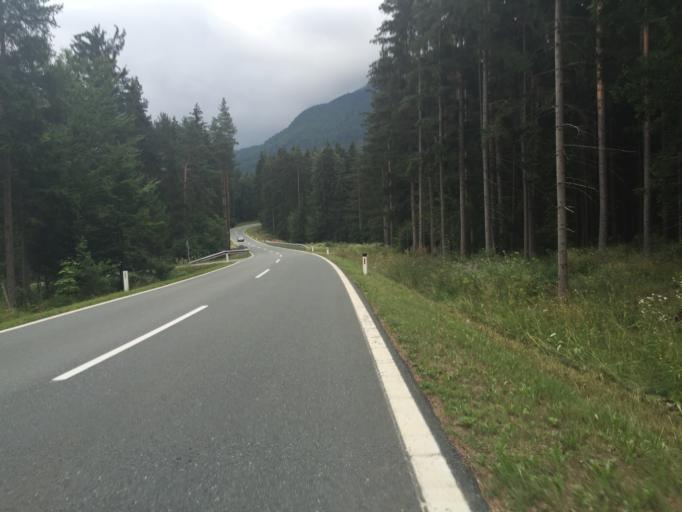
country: AT
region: Carinthia
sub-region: Politischer Bezirk Volkermarkt
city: Feistritz ob Bleiburg
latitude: 46.5484
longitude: 14.7710
